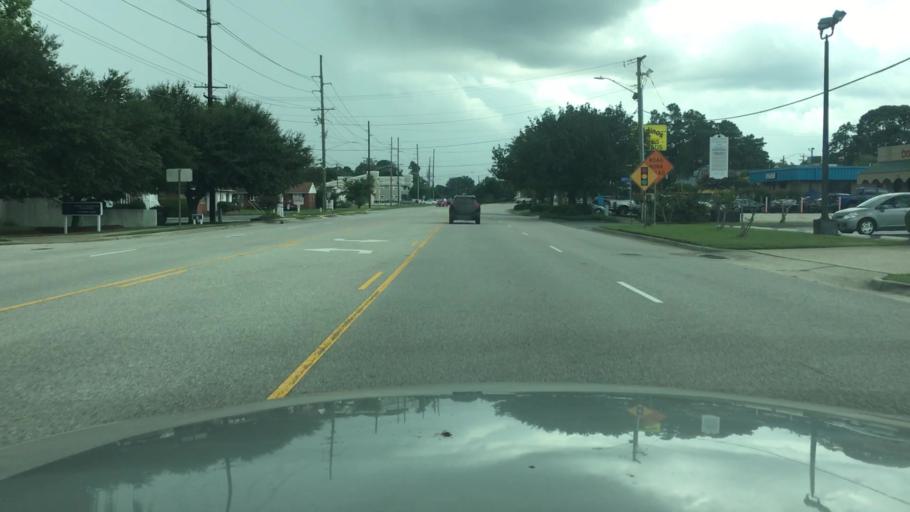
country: US
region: North Carolina
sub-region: Cumberland County
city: Fayetteville
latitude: 35.0412
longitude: -78.9341
